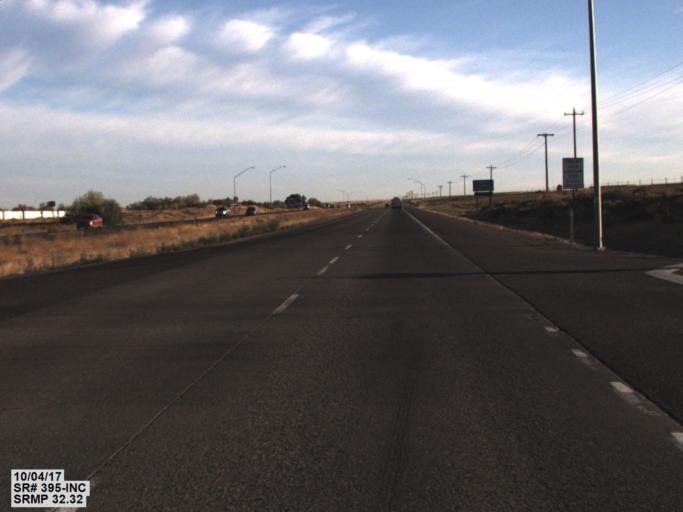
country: US
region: Washington
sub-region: Franklin County
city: Pasco
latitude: 46.3861
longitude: -119.0676
